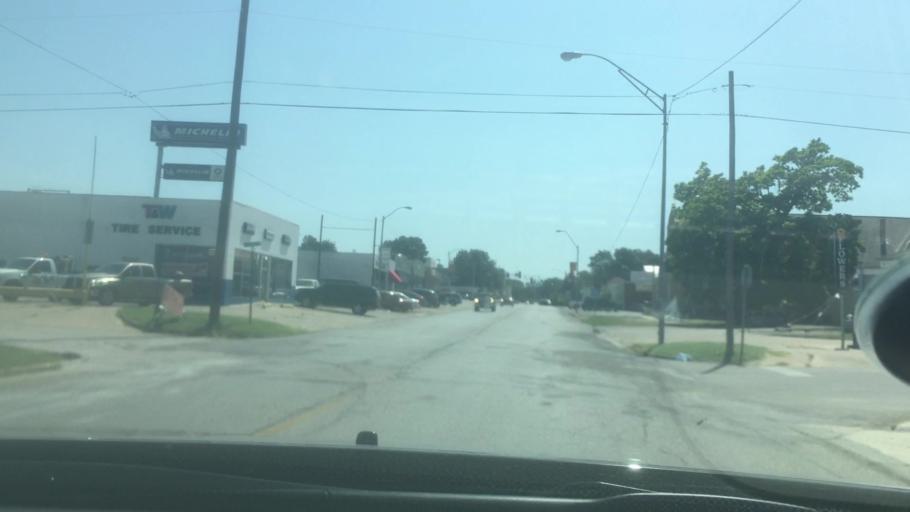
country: US
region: Oklahoma
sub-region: Pontotoc County
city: Ada
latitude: 34.7745
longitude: -96.6724
